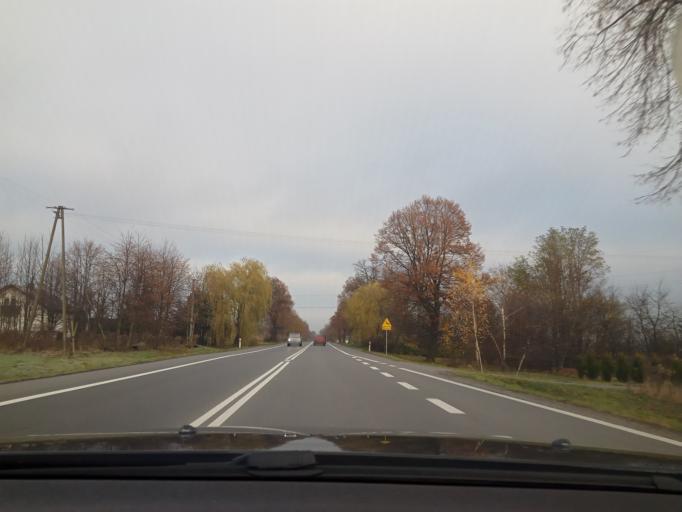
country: PL
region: Lesser Poland Voivodeship
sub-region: Powiat miechowski
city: Miechow
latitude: 50.3297
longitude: 20.0338
